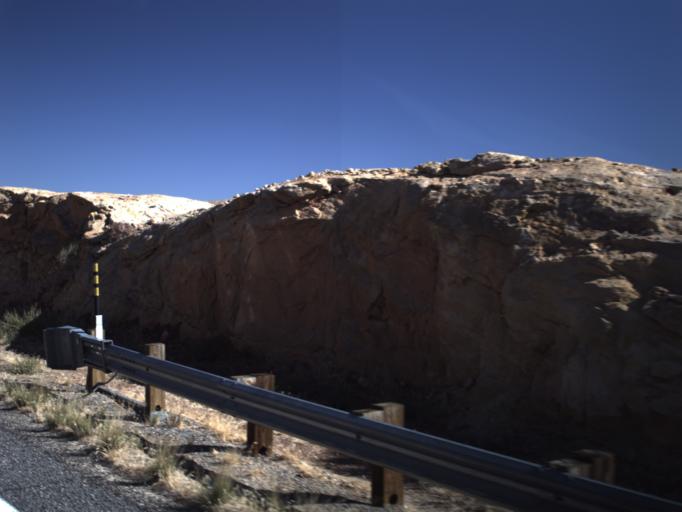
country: US
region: Utah
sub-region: San Juan County
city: Blanding
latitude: 37.9170
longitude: -110.3881
